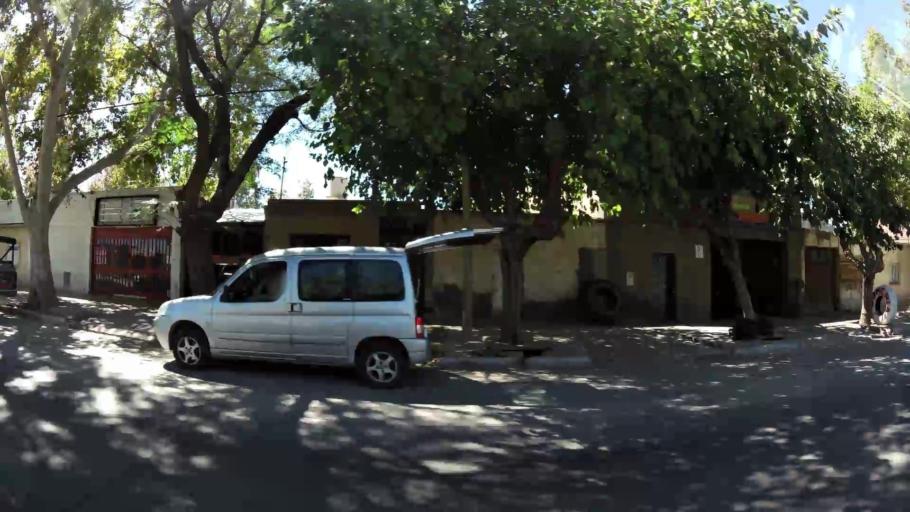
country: AR
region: San Juan
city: Villa Krause
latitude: -31.5584
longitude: -68.5238
